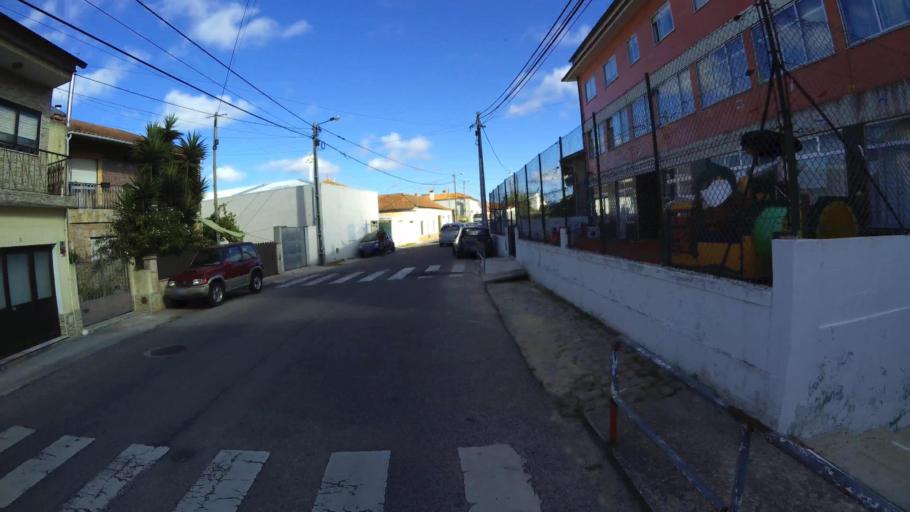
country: PT
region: Aveiro
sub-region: Aveiro
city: Aveiro
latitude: 40.6419
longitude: -8.6228
